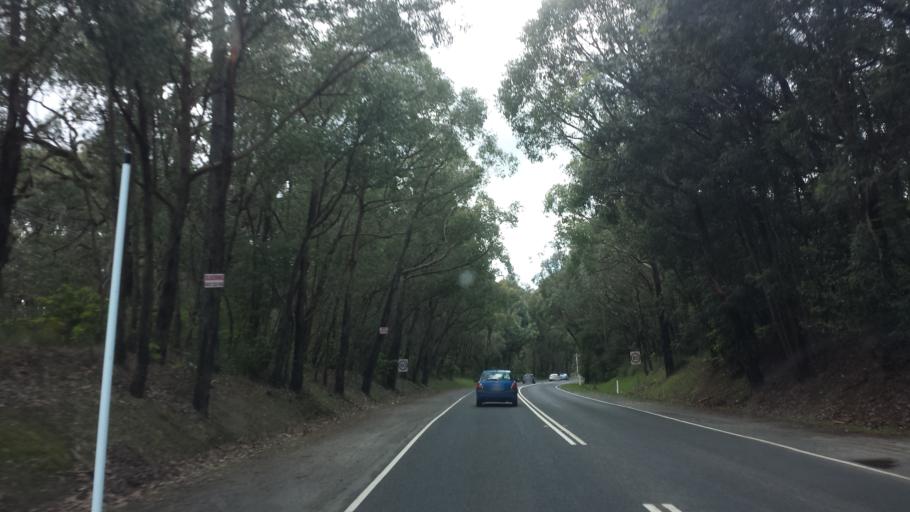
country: AU
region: Victoria
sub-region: Yarra Ranges
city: Selby
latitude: -37.9368
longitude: 145.4048
